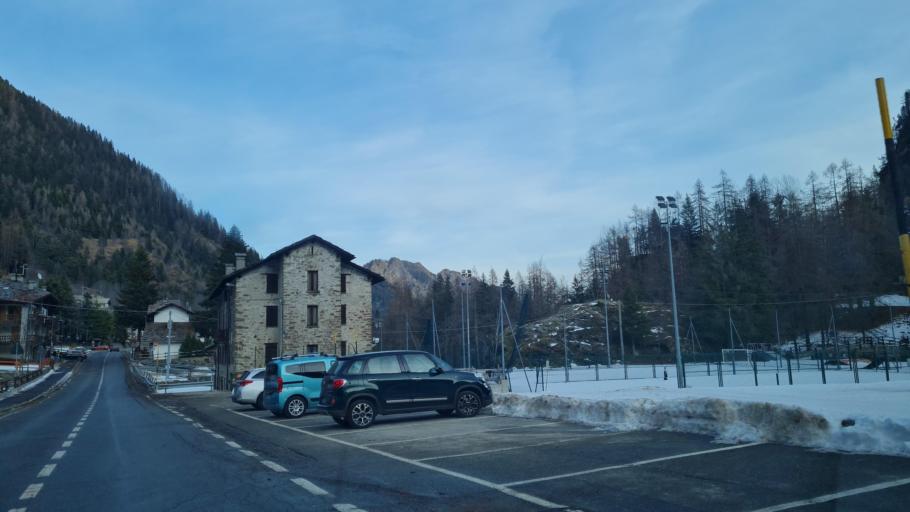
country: IT
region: Aosta Valley
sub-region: Valle d'Aosta
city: Champorcher
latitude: 45.6222
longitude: 7.6160
